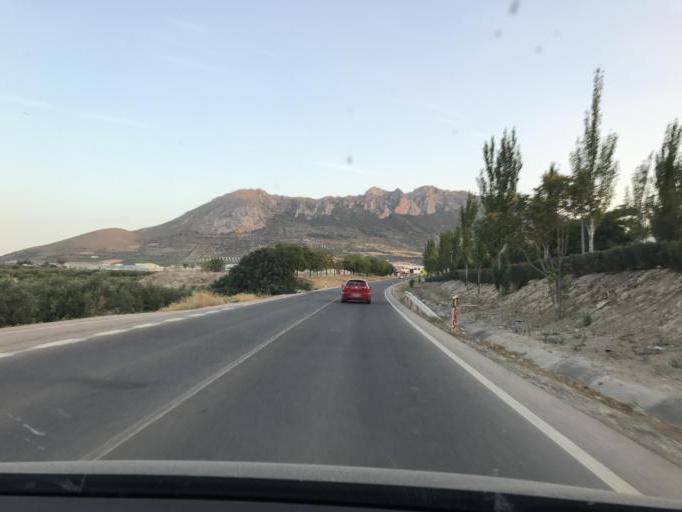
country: ES
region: Andalusia
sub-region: Provincia de Jaen
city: Jodar
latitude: 37.8416
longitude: -3.3441
